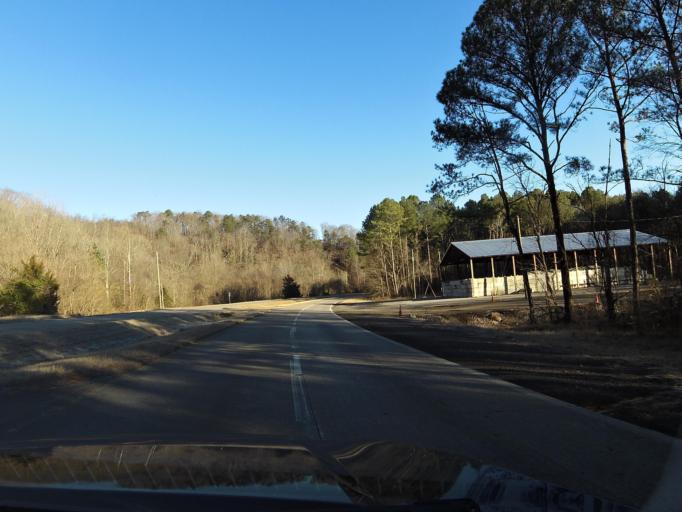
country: US
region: Alabama
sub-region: Morgan County
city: Falkville
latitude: 34.3188
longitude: -86.9016
